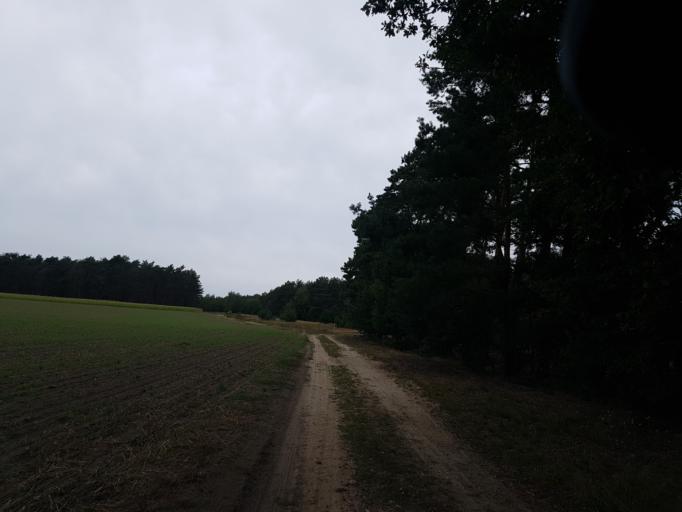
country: DE
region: Brandenburg
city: Finsterwalde
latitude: 51.6133
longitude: 13.6416
